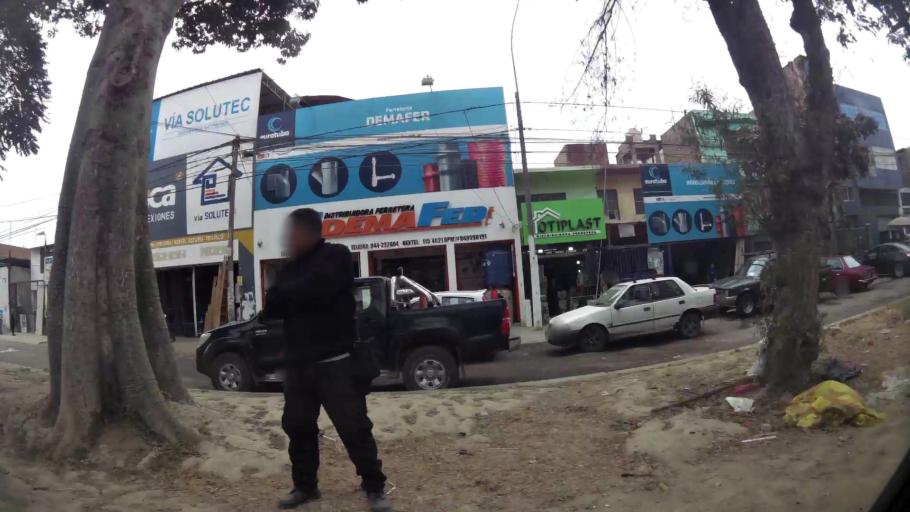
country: PE
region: La Libertad
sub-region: Provincia de Trujillo
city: Trujillo
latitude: -8.1134
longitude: -79.0170
